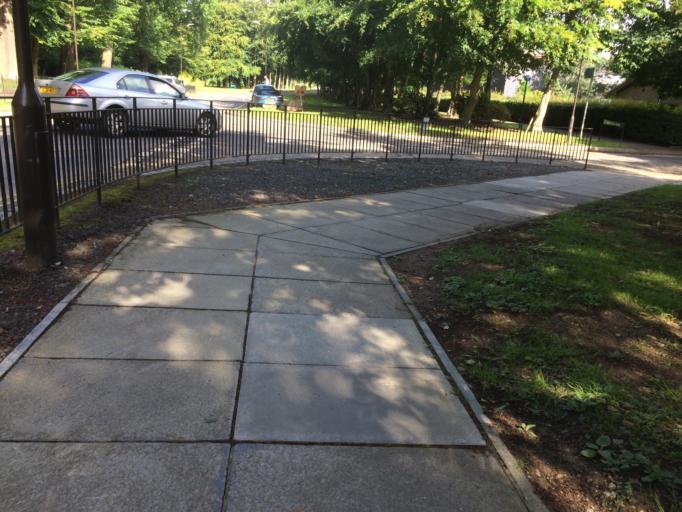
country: GB
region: Scotland
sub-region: Edinburgh
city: Currie
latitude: 55.9112
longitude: -3.3168
